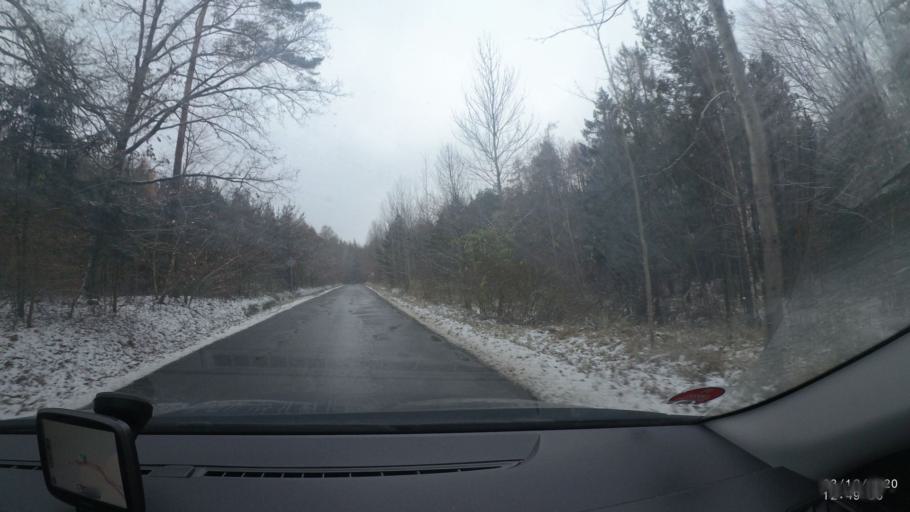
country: CZ
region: Central Bohemia
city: Nove Straseci
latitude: 50.1667
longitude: 13.8722
